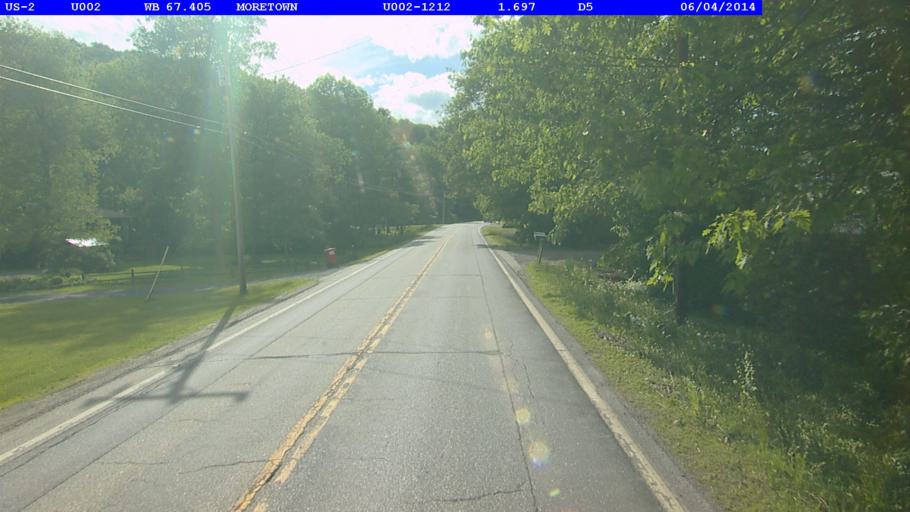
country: US
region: Vermont
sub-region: Washington County
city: Waterbury
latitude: 44.3122
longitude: -72.7206
